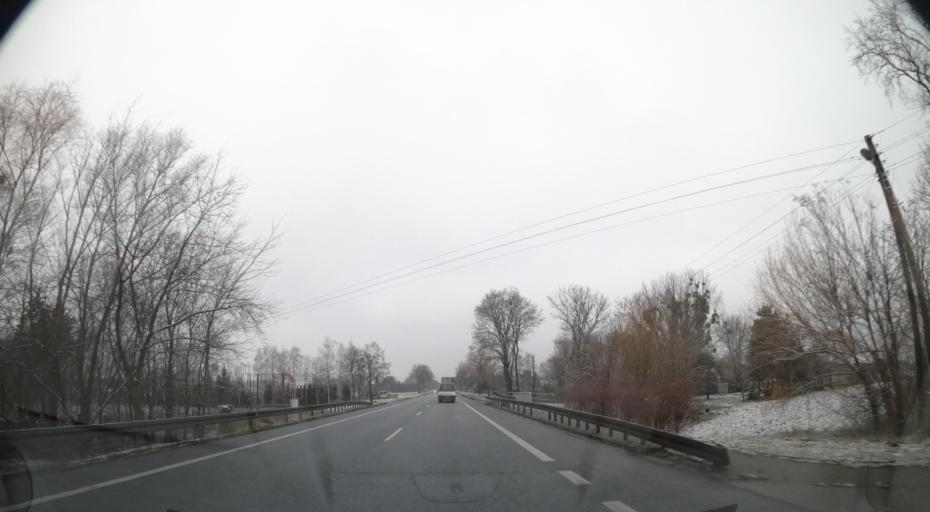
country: PL
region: Masovian Voivodeship
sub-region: Powiat sochaczewski
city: Paprotnia
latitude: 52.2074
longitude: 20.4796
